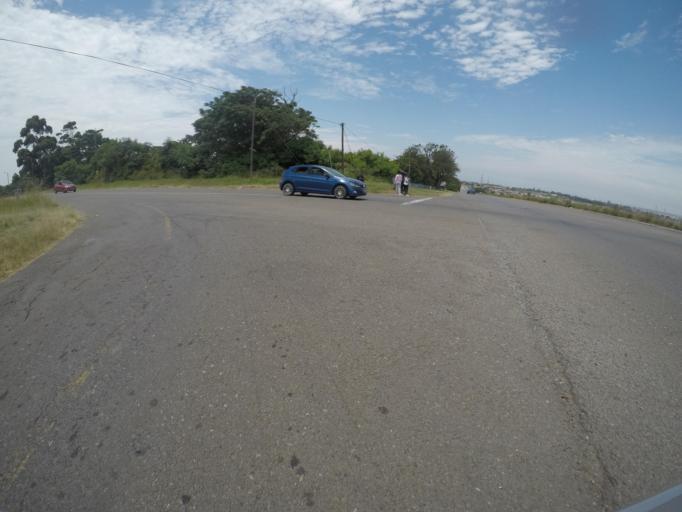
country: ZA
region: Eastern Cape
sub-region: Buffalo City Metropolitan Municipality
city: East London
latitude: -32.9733
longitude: 27.8530
